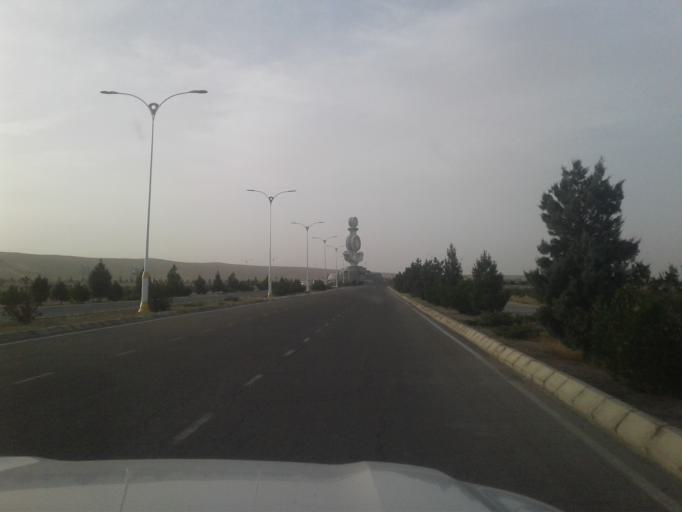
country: TM
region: Balkan
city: Turkmenbasy
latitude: 40.0421
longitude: 52.9815
